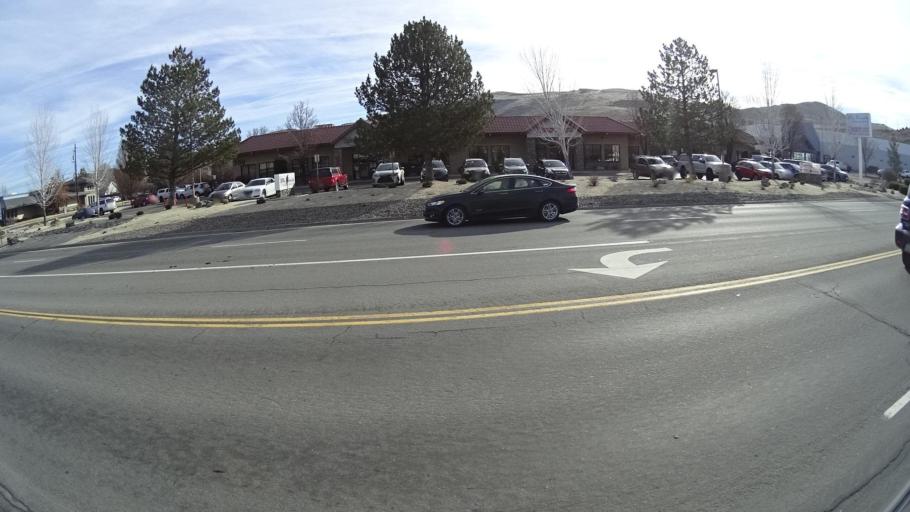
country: US
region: Nevada
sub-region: Washoe County
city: Sparks
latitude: 39.5414
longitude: -119.7036
